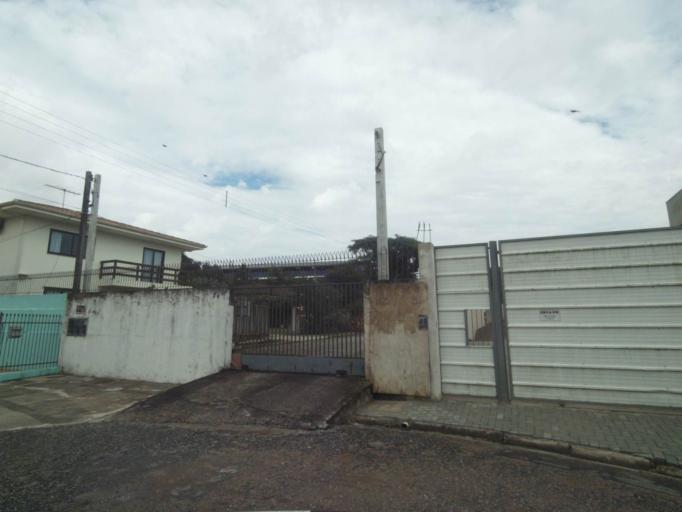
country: BR
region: Parana
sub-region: Pinhais
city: Pinhais
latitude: -25.4764
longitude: -49.2037
